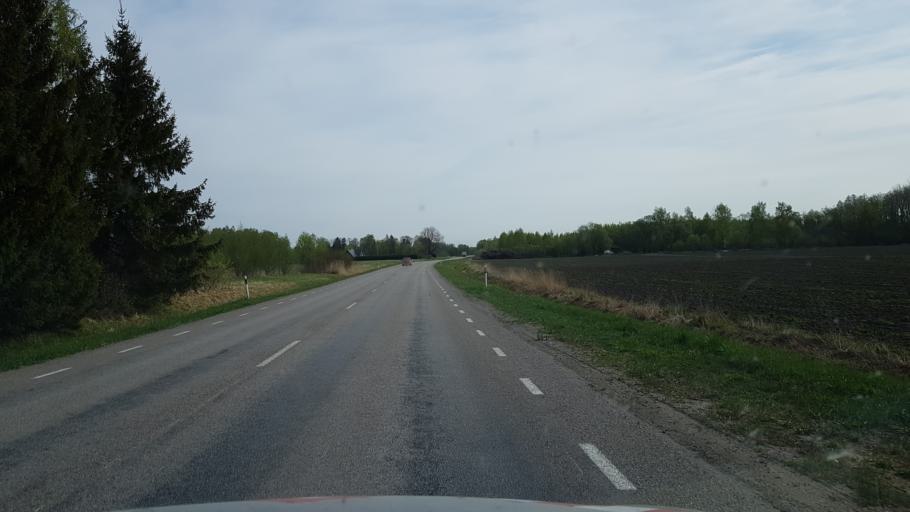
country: EE
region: Paernumaa
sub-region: Audru vald
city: Audru
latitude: 58.3943
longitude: 24.2831
